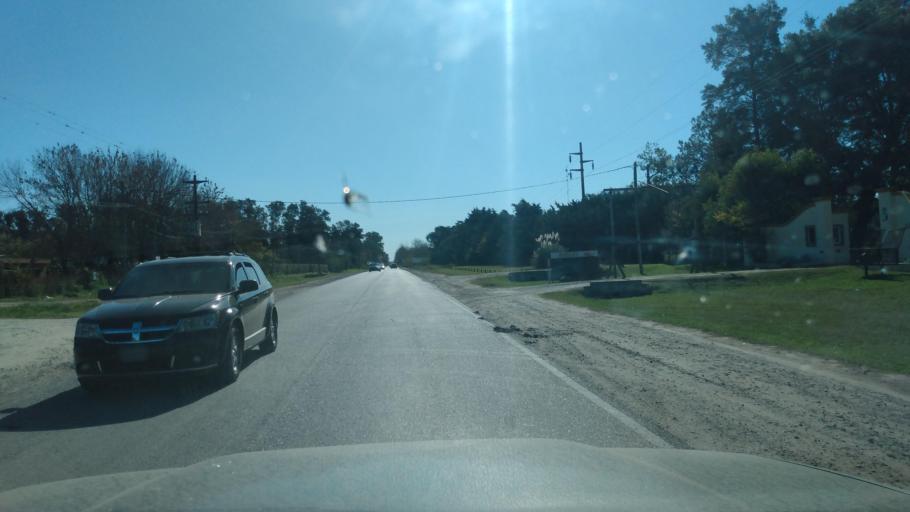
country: AR
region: Buenos Aires
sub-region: Partido de Lujan
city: Lujan
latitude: -34.5429
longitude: -59.1583
